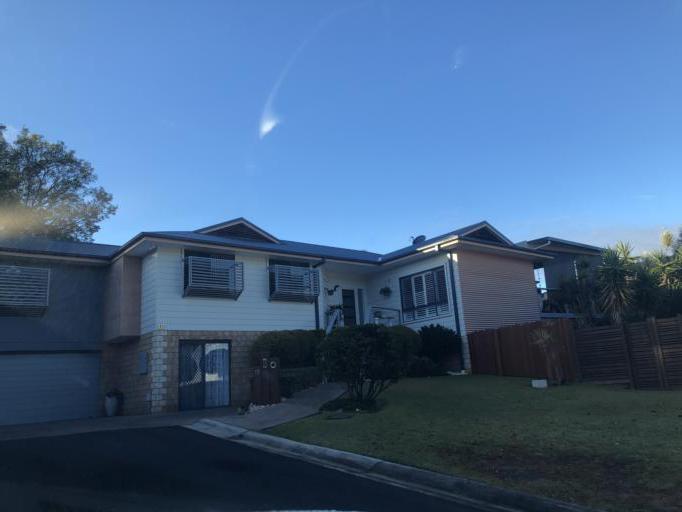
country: AU
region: New South Wales
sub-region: Coffs Harbour
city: Coffs Harbour
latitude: -30.2935
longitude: 153.1297
